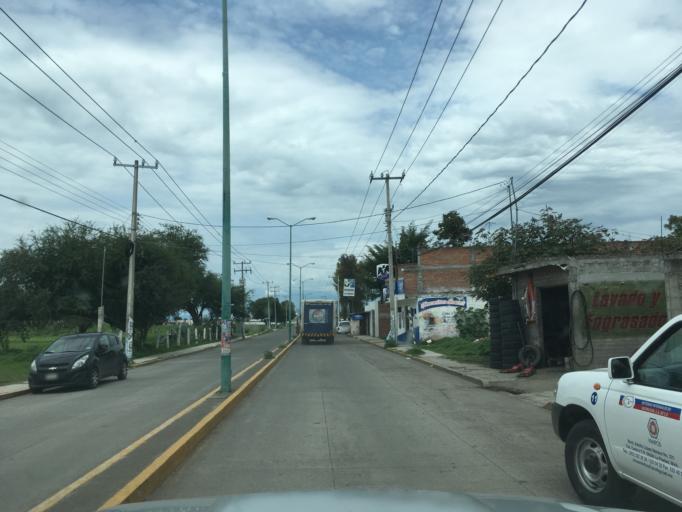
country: MX
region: Michoacan
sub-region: Tarimbaro
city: Meson Nuevo (Canada de la Magdalena)
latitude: 19.7962
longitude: -101.1713
